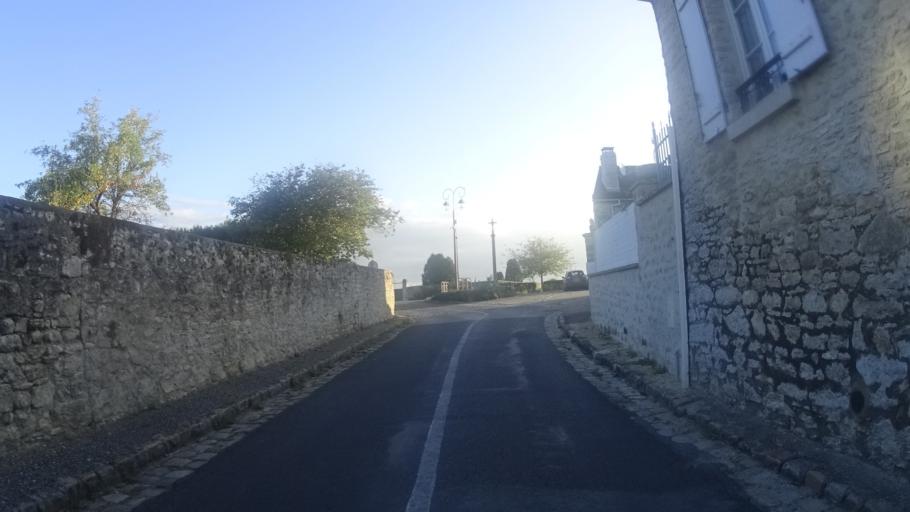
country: FR
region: Picardie
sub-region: Departement de l'Oise
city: Chamant
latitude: 49.1813
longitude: 2.6716
